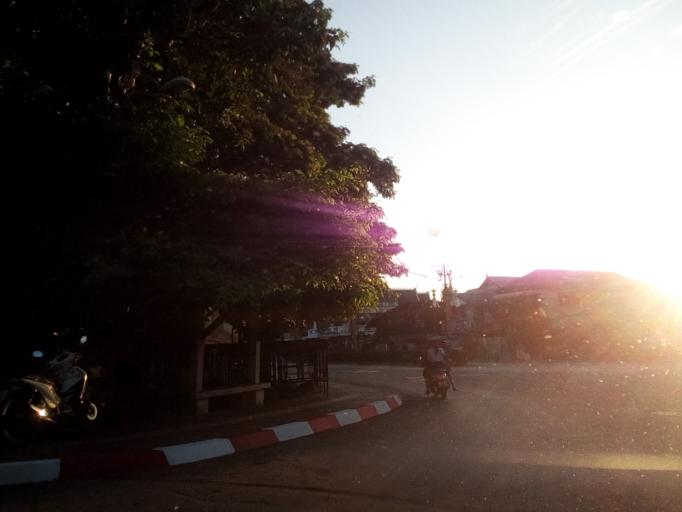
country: TH
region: Lamphun
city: Lamphun
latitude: 18.5805
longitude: 99.0099
